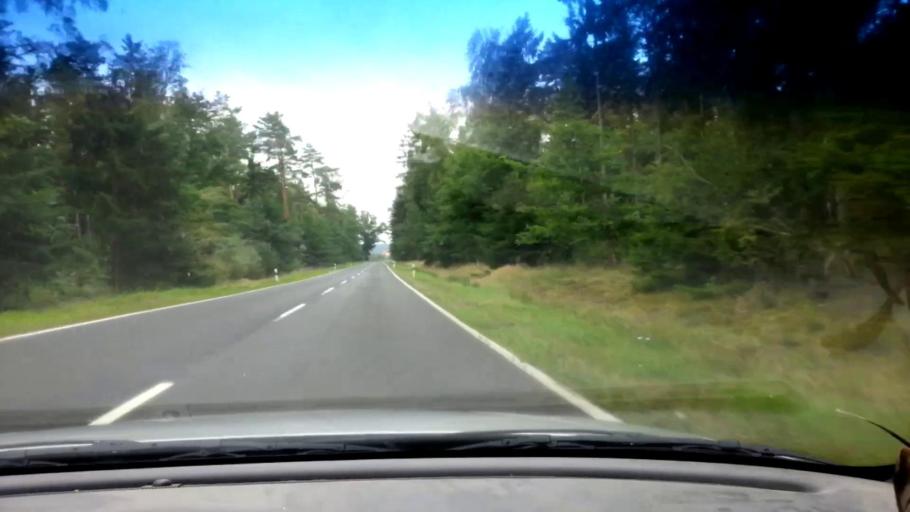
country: DE
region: Bavaria
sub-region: Upper Palatinate
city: Waldsassen
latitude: 50.0182
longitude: 12.3120
